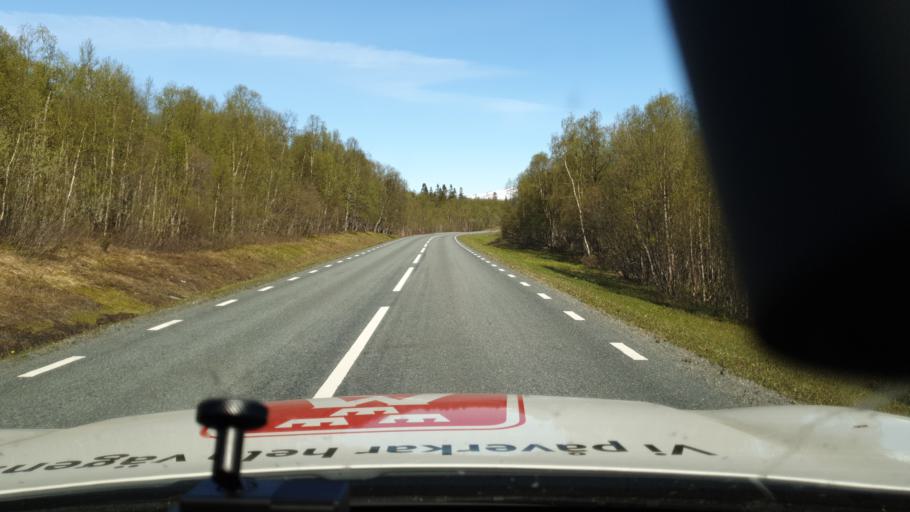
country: NO
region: Nordland
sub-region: Rana
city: Mo i Rana
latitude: 65.7674
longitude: 15.1134
